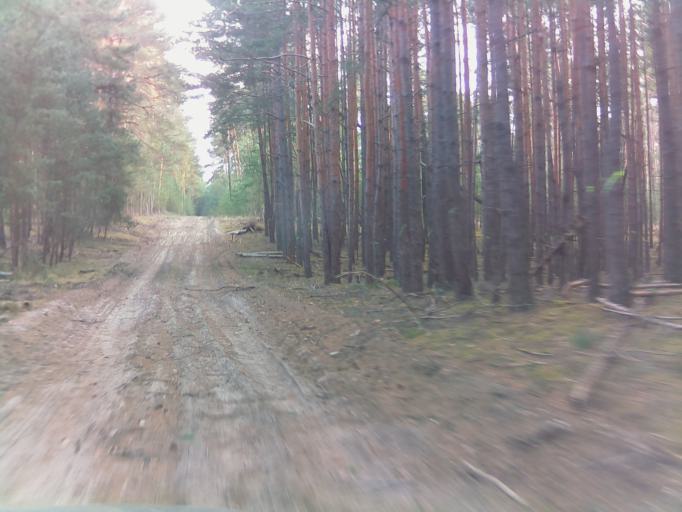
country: DE
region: Brandenburg
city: Tauer
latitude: 51.9771
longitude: 14.4545
